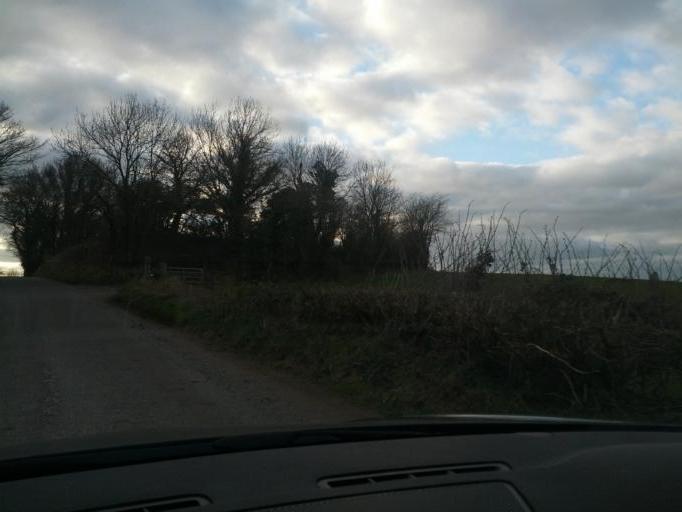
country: IE
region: Leinster
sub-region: An Iarmhi
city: Athlone
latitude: 53.3222
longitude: -7.9625
